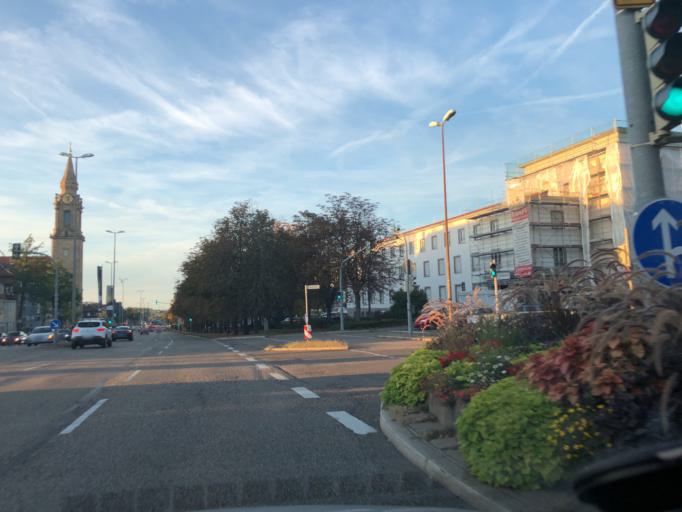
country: DE
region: Baden-Wuerttemberg
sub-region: Regierungsbezirk Stuttgart
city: Ludwigsburg
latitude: 48.8889
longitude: 9.1946
